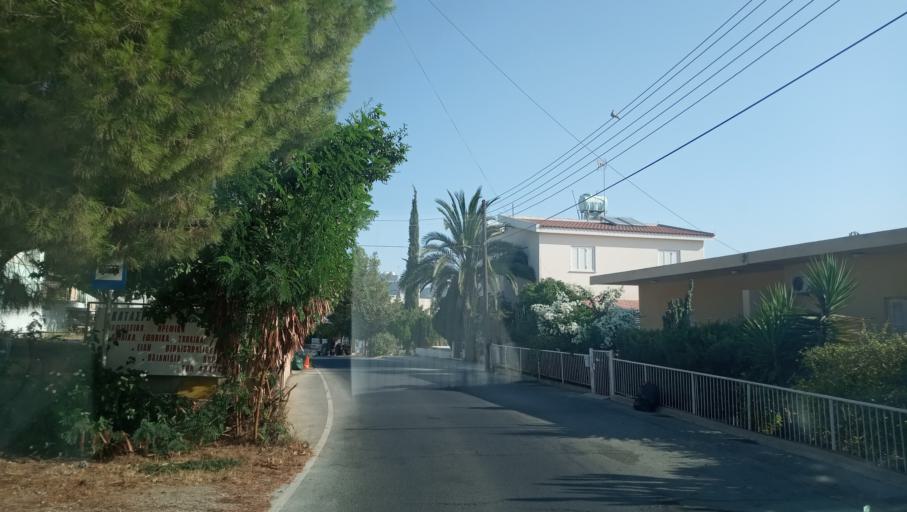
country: CY
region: Lefkosia
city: Geri
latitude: 35.1104
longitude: 33.4227
